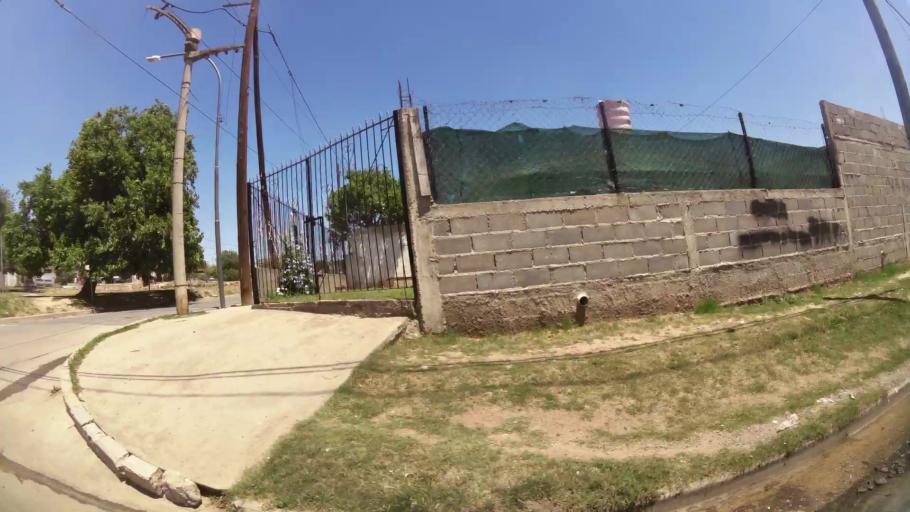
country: AR
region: Cordoba
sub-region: Departamento de Capital
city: Cordoba
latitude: -31.4189
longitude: -64.1193
